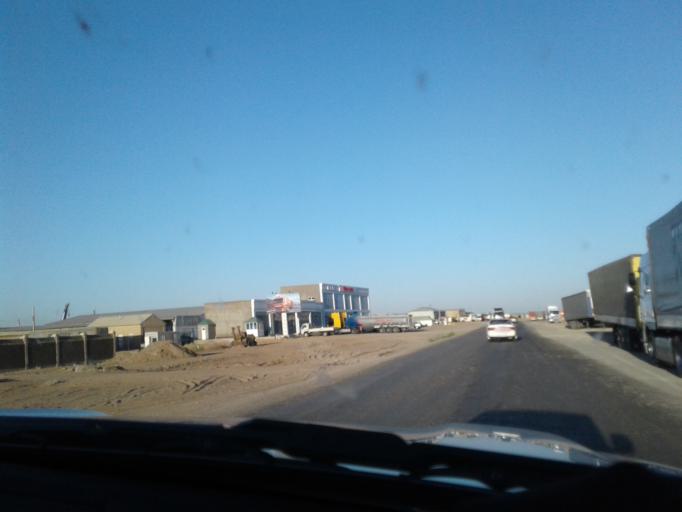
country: TM
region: Mary
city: Mary
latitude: 37.5658
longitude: 61.8149
